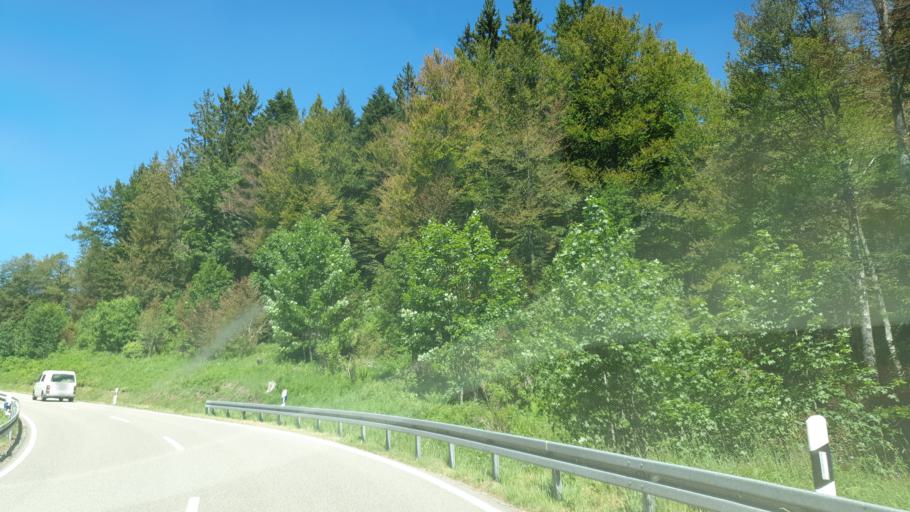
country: DE
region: Baden-Wuerttemberg
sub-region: Freiburg Region
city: Wieden
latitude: 47.8716
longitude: 7.9147
